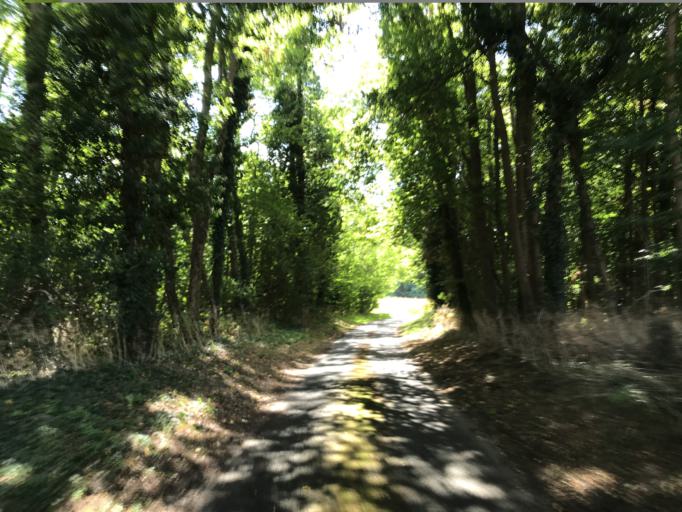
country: FR
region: Haute-Normandie
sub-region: Departement de l'Eure
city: Saint-Just
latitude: 49.1499
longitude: 1.4060
